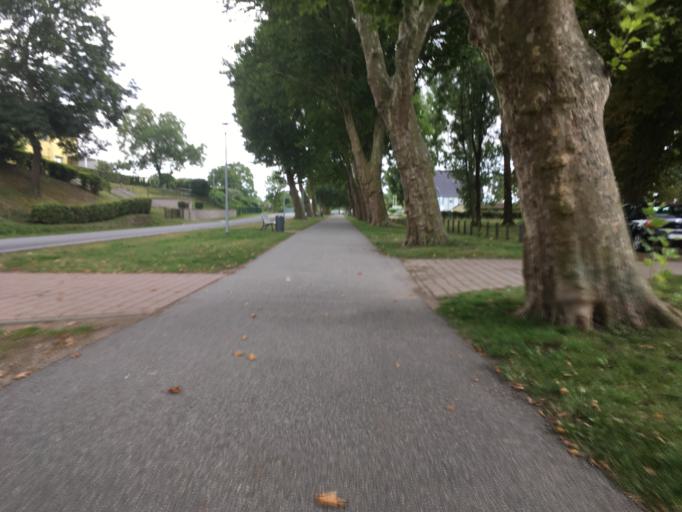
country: DE
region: Brandenburg
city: Prenzlau
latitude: 53.3049
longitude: 13.8623
